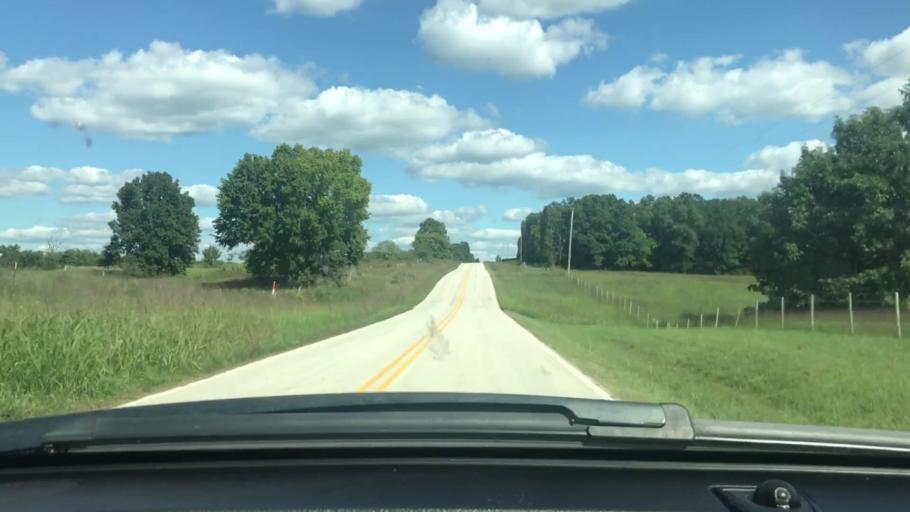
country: US
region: Missouri
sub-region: Wright County
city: Hartville
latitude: 37.3770
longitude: -92.4138
